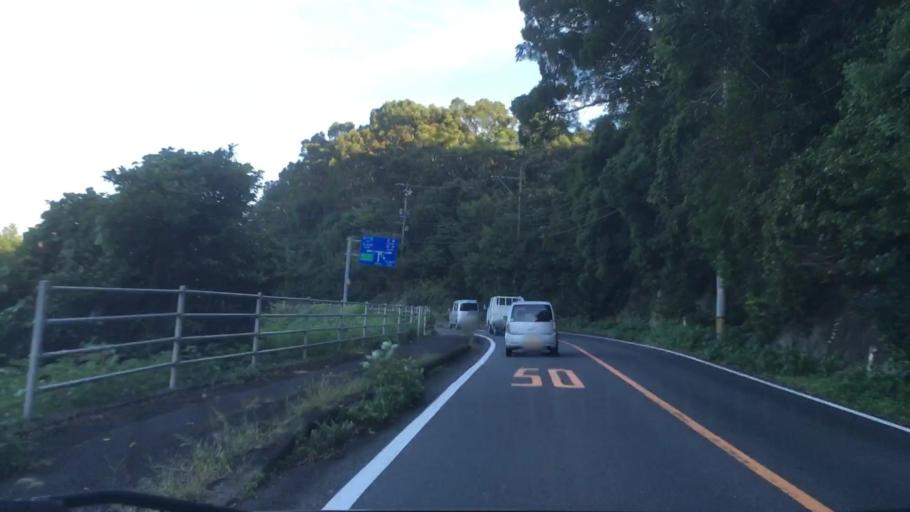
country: JP
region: Nagasaki
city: Sasebo
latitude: 33.0446
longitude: 129.7379
